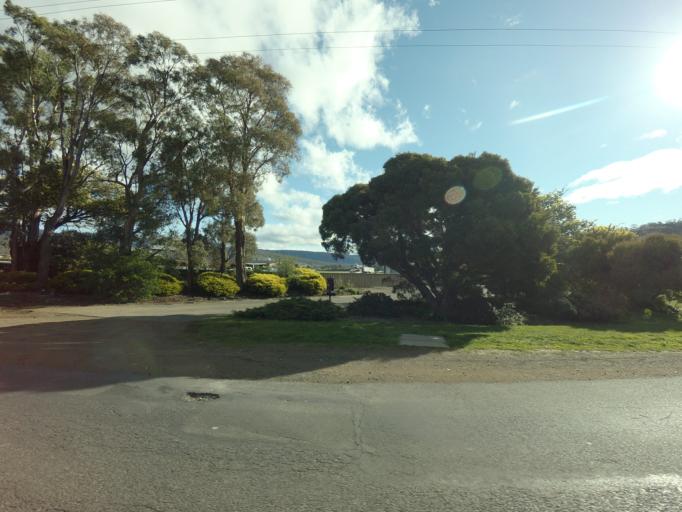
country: AU
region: Tasmania
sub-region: Derwent Valley
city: New Norfolk
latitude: -42.7654
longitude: 147.0461
